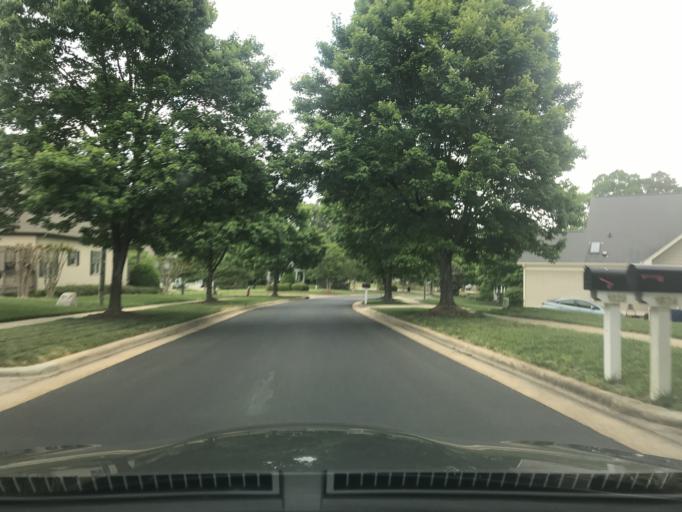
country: US
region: North Carolina
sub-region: Wake County
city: Wake Forest
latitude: 35.9140
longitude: -78.5774
